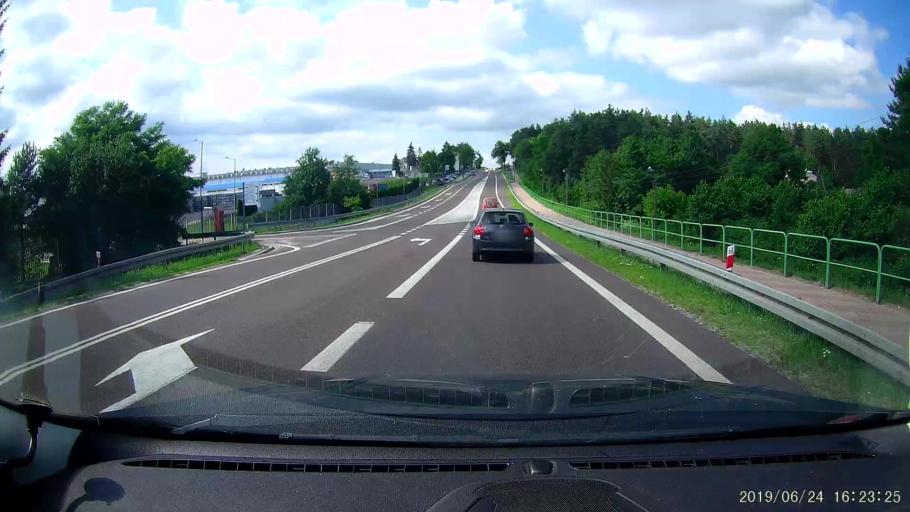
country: PL
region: Lublin Voivodeship
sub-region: Powiat tomaszowski
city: Tomaszow Lubelski
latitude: 50.4314
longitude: 23.4216
